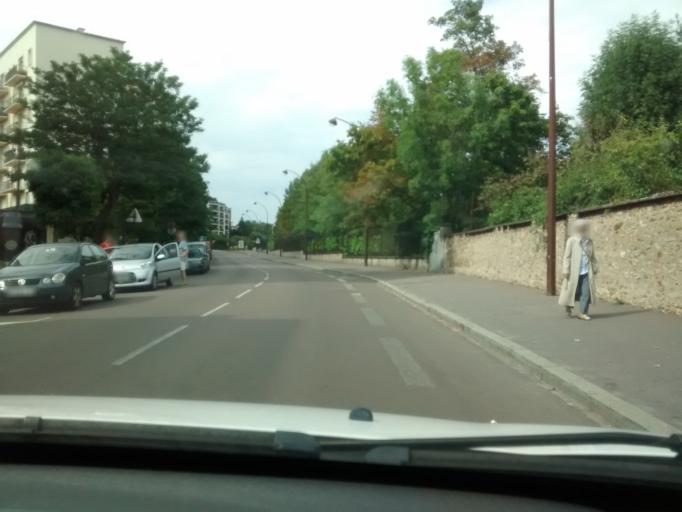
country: FR
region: Ile-de-France
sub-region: Departement des Yvelines
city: Viroflay
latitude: 48.8008
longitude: 2.1535
